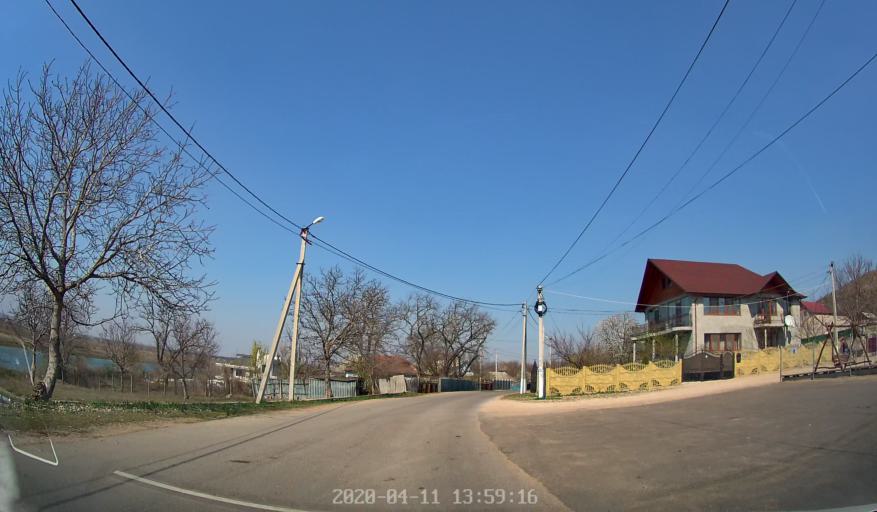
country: MD
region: Chisinau
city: Vadul lui Voda
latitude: 47.0819
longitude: 29.1307
